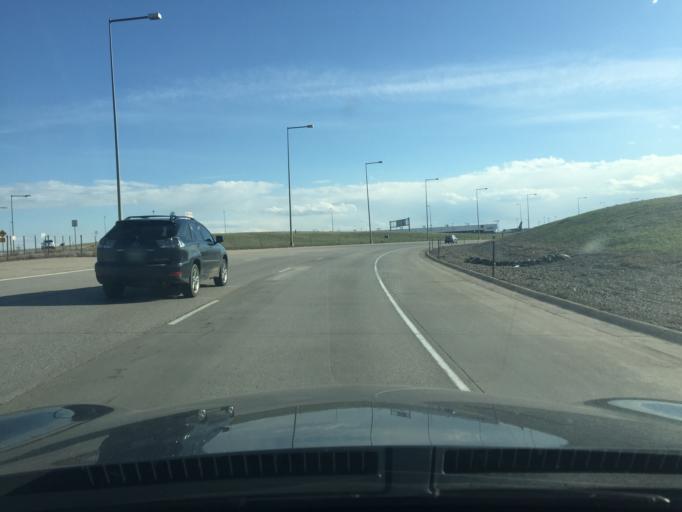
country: US
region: Colorado
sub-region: Weld County
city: Lochbuie
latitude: 39.8361
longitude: -104.6765
